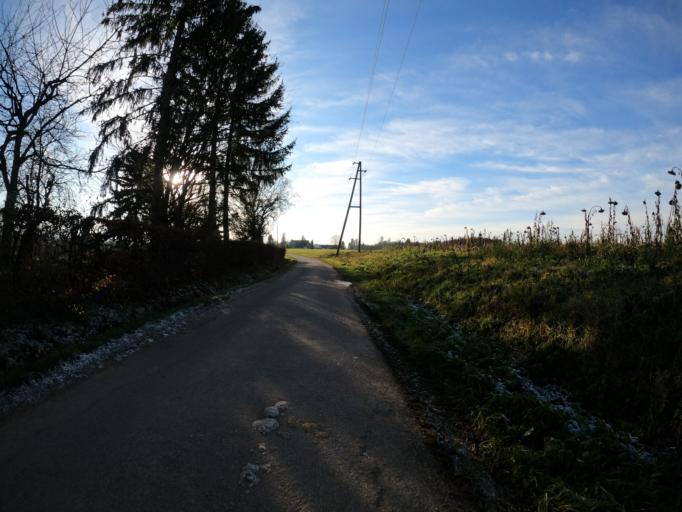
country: DE
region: Baden-Wuerttemberg
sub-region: Regierungsbezirk Stuttgart
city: Heiningen
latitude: 48.6829
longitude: 9.6194
